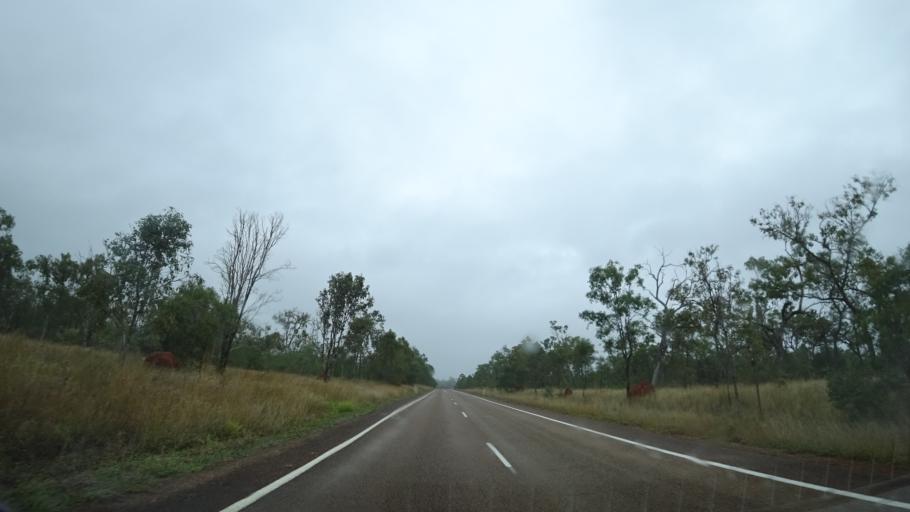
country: AU
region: Queensland
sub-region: Tablelands
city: Ravenshoe
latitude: -17.6957
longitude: 145.2159
